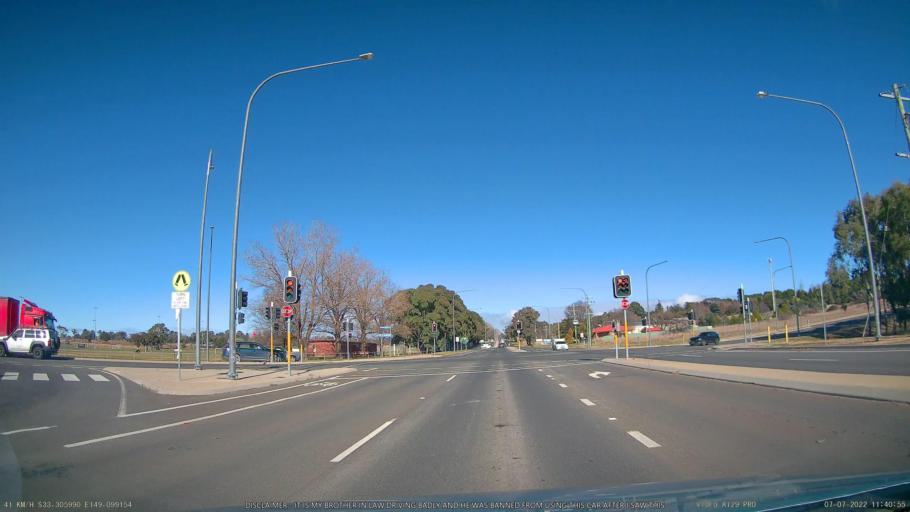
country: AU
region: New South Wales
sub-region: Orange Municipality
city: Orange
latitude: -33.3062
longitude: 149.0990
